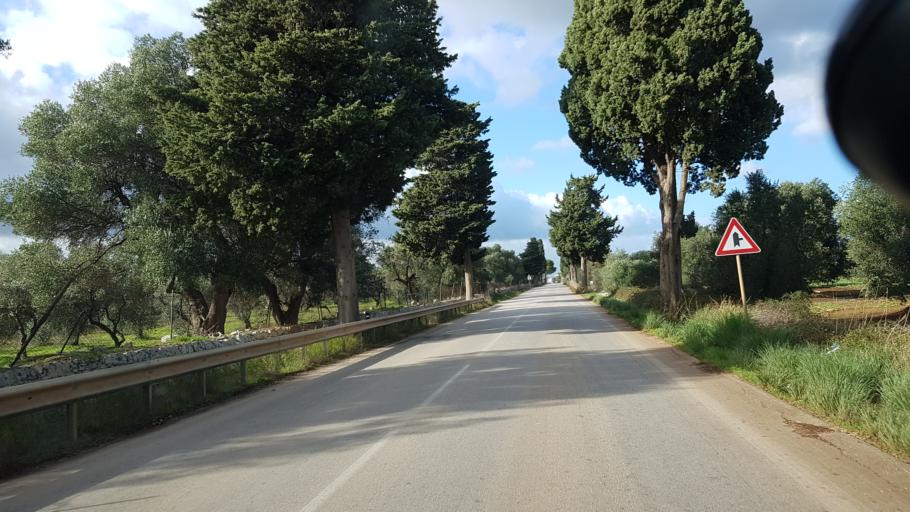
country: IT
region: Apulia
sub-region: Provincia di Brindisi
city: Montalbano
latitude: 40.7779
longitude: 17.4903
